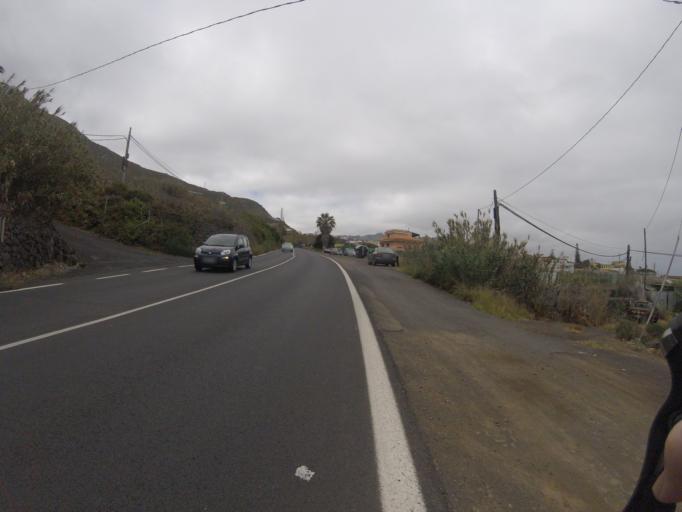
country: ES
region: Canary Islands
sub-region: Provincia de Santa Cruz de Tenerife
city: Tegueste
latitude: 28.5415
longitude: -16.3579
